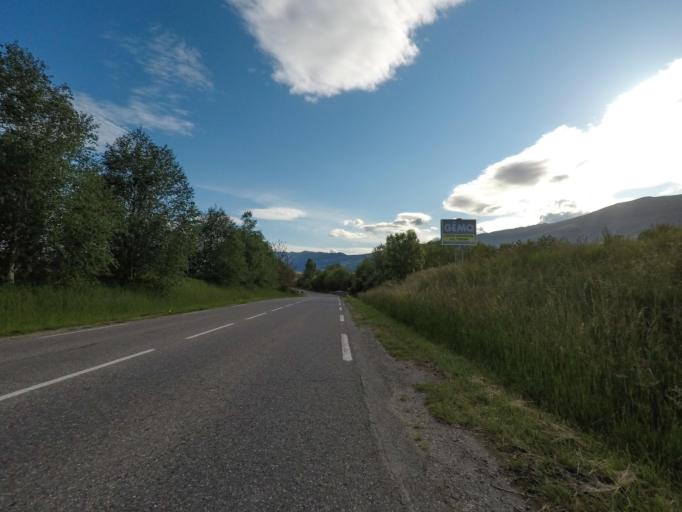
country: FR
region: Rhone-Alpes
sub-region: Departement de l'Ain
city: Sergy
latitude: 46.2321
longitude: 6.0013
